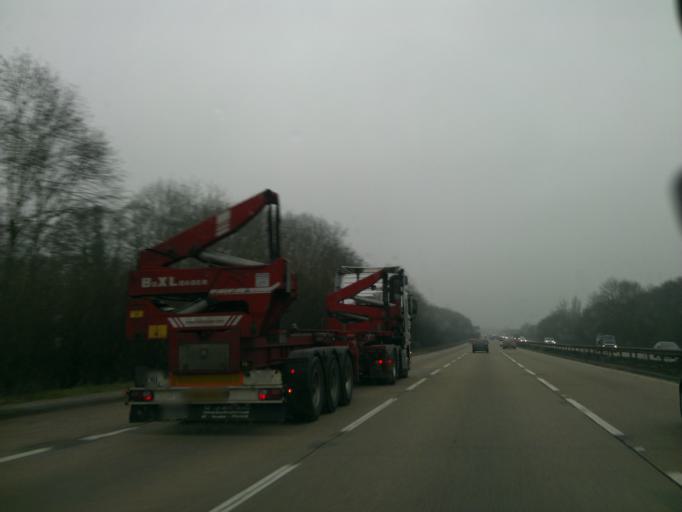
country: GB
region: England
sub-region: Essex
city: Eight Ash Green
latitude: 51.8842
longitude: 0.7984
